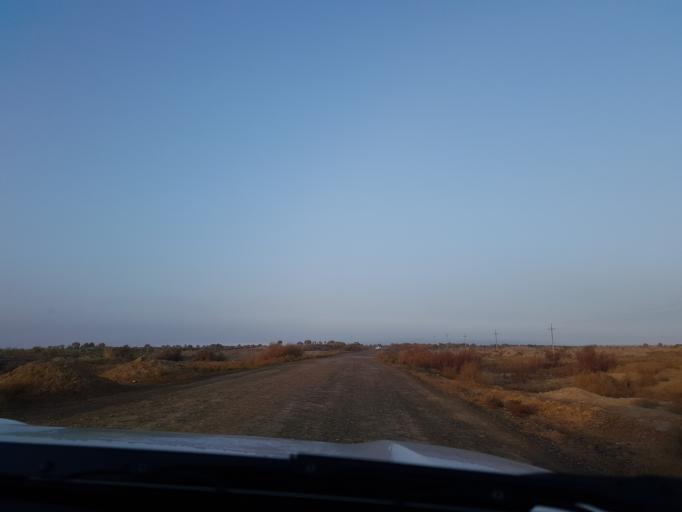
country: TM
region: Dasoguz
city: Koeneuergench
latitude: 41.8444
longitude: 58.5944
